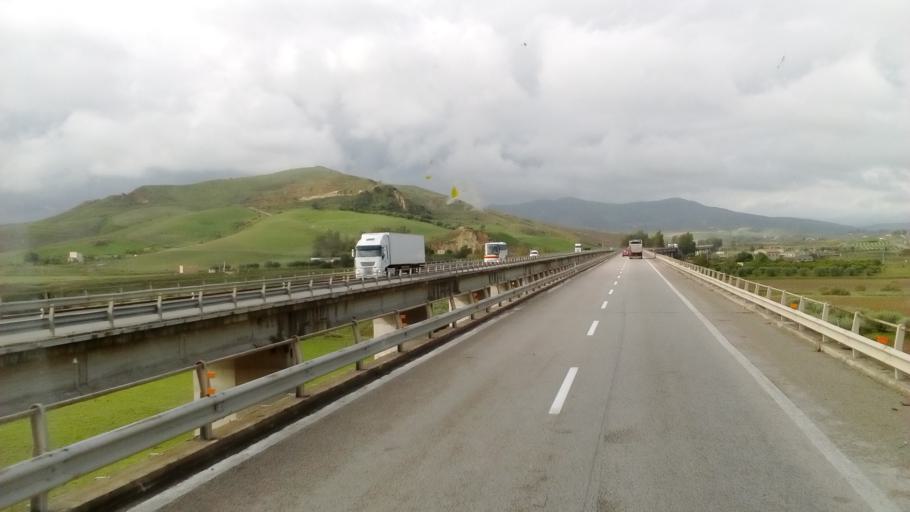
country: IT
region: Sicily
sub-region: Enna
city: Assoro
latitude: 37.5733
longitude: 14.4534
